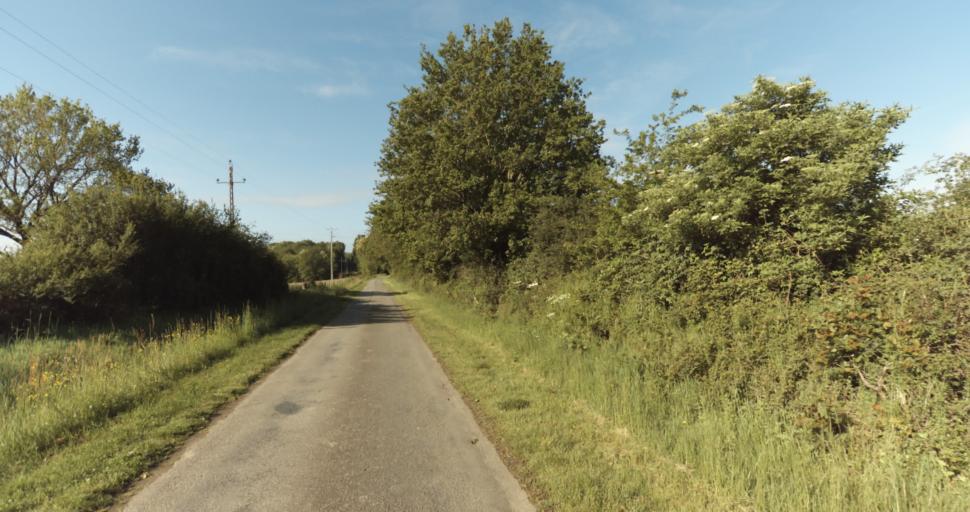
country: FR
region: Limousin
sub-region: Departement de la Haute-Vienne
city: Solignac
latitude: 45.7408
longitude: 1.2662
